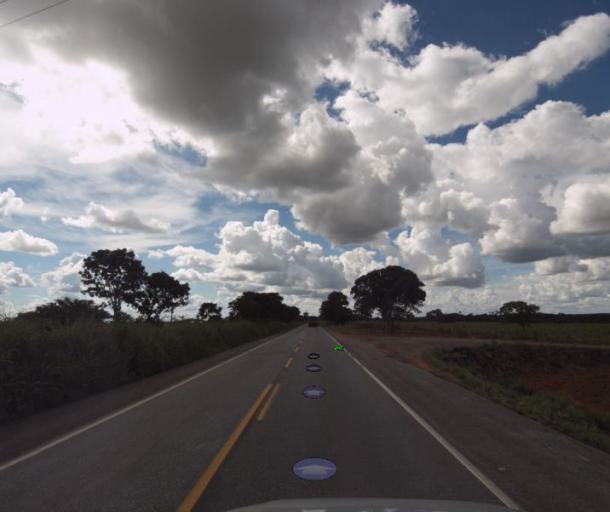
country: BR
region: Goias
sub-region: Porangatu
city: Porangatu
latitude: -13.2903
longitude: -49.1248
